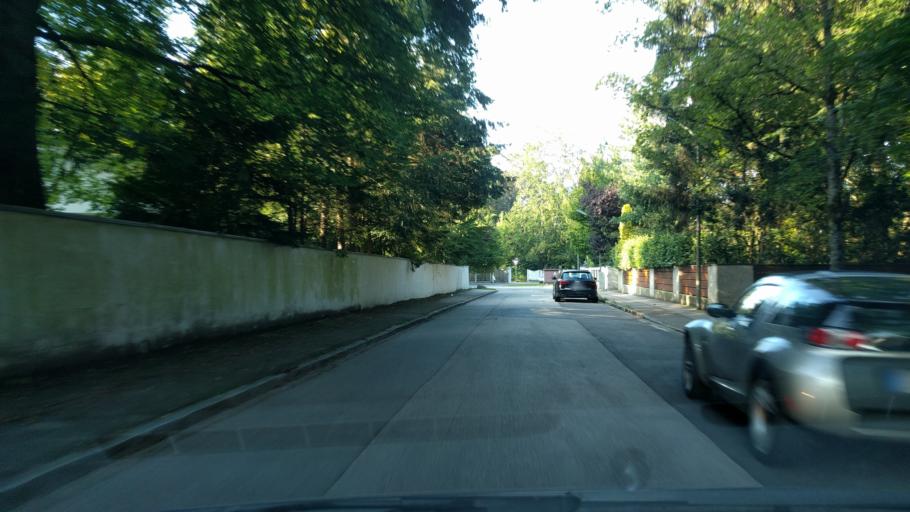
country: DE
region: Bavaria
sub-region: Upper Bavaria
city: Grunwald
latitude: 48.0501
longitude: 11.5438
